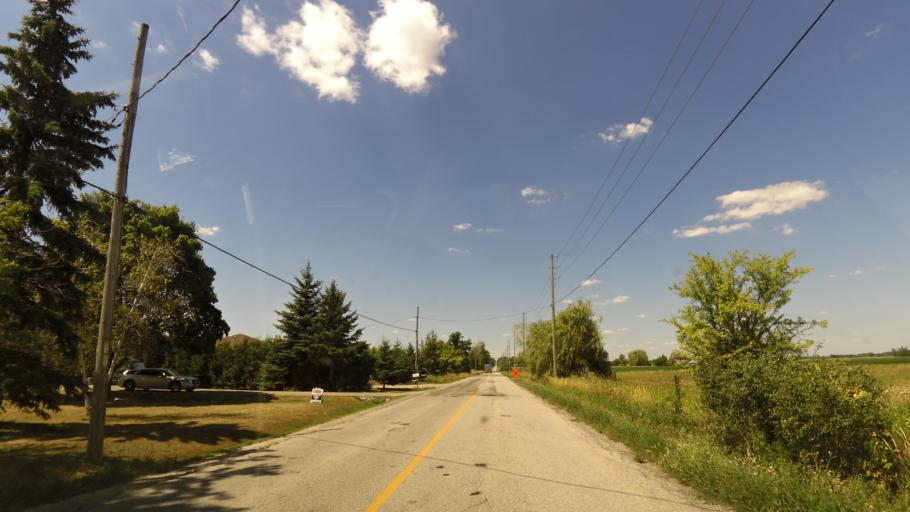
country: CA
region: Ontario
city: Brampton
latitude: 43.6054
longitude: -79.8188
